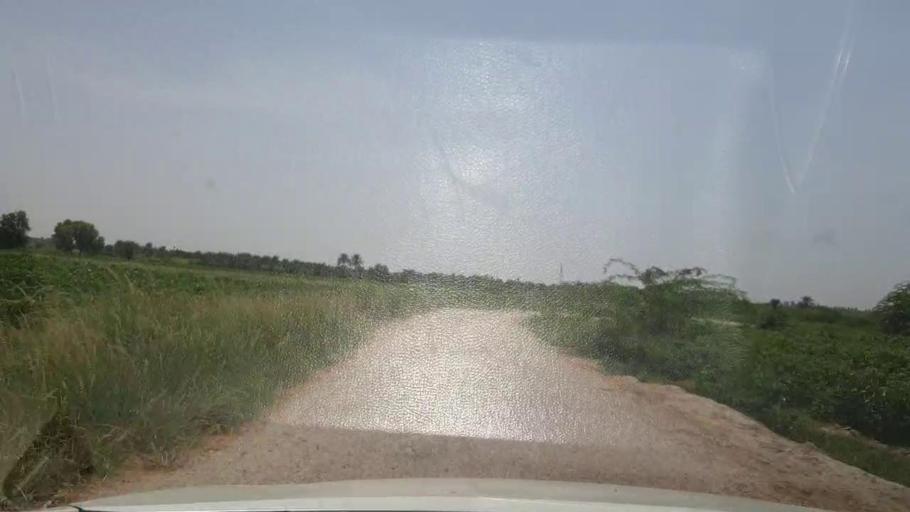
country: PK
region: Sindh
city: Bozdar
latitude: 27.2158
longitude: 68.6584
